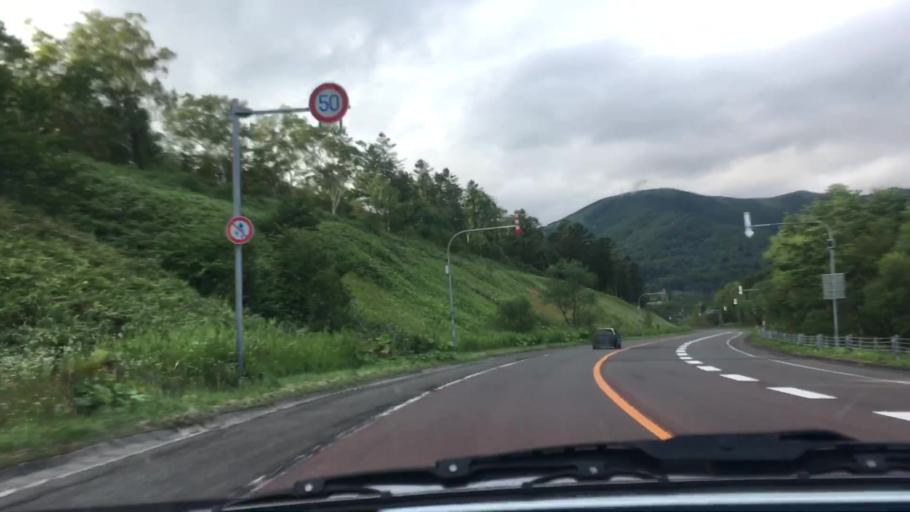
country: JP
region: Hokkaido
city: Shimo-furano
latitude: 43.1294
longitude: 142.7584
